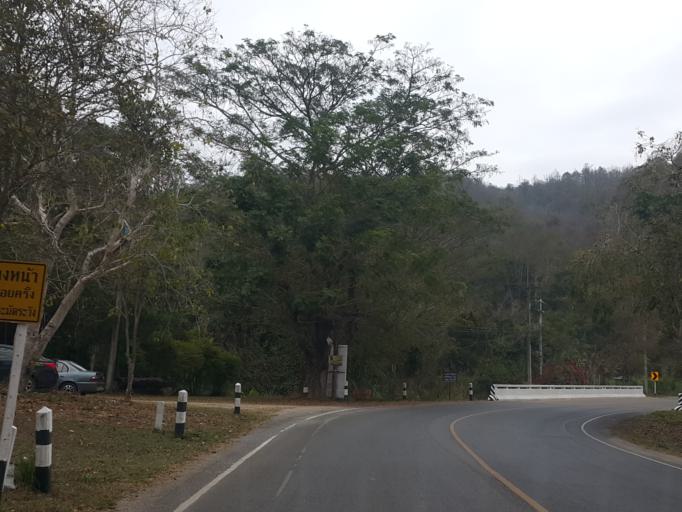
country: TH
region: Chiang Mai
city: Hang Dong
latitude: 18.7641
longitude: 98.8747
